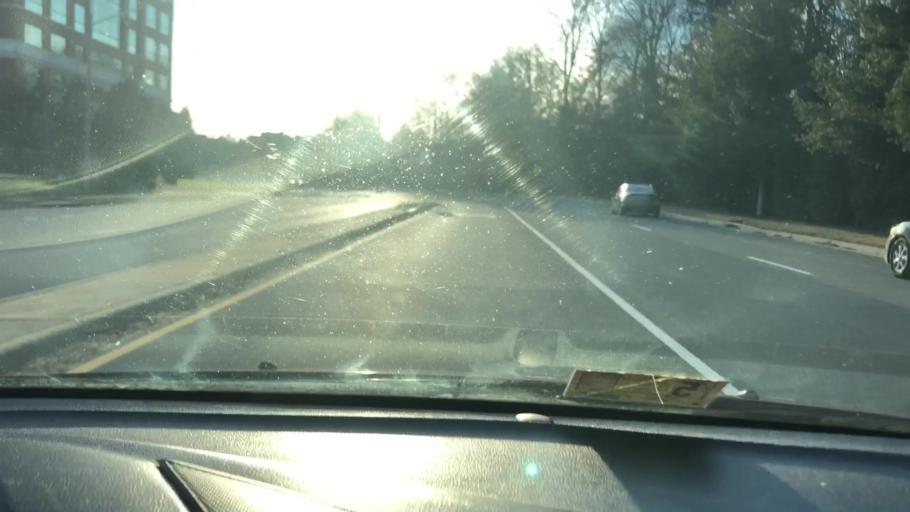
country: US
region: Virginia
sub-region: Fairfax County
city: Franconia
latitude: 38.7720
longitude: -77.1411
